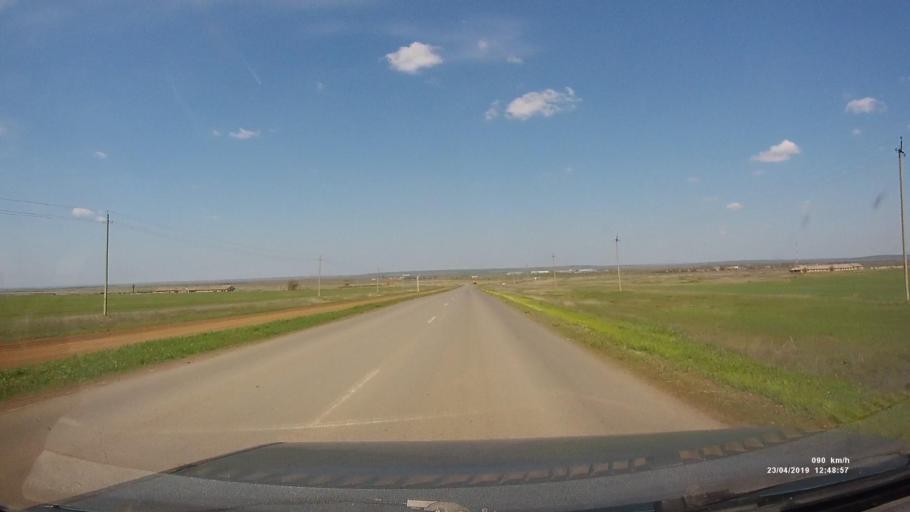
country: RU
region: Kalmykiya
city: Yashalta
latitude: 46.5310
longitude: 42.6389
